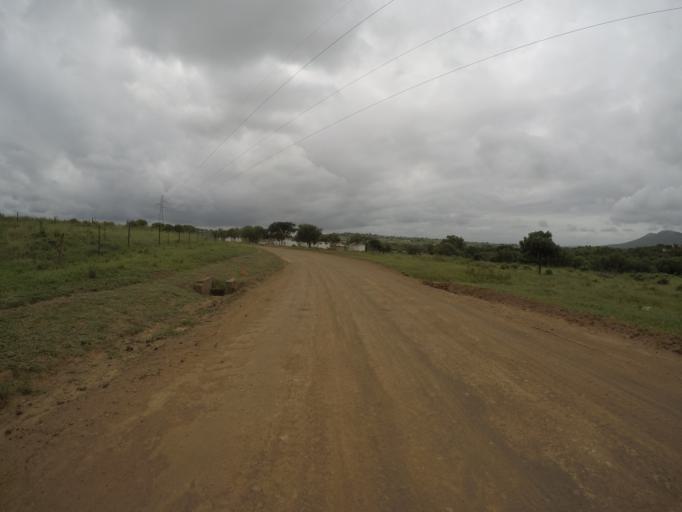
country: ZA
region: KwaZulu-Natal
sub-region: uThungulu District Municipality
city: Empangeni
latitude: -28.5930
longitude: 31.8409
